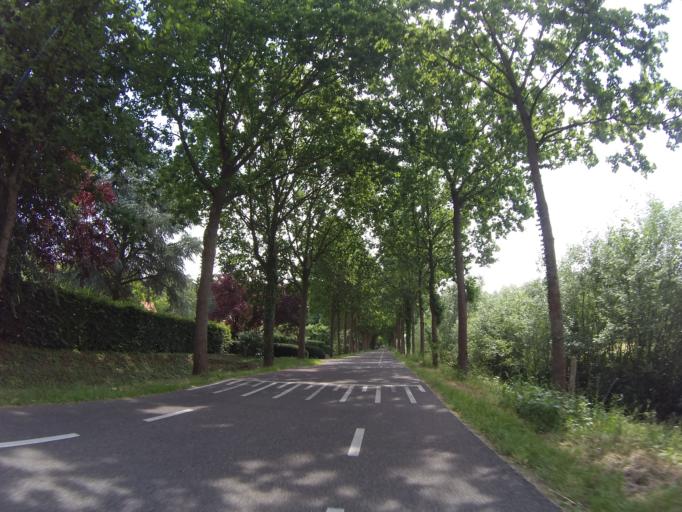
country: NL
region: Utrecht
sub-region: Gemeente Bunnik
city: Bunnik
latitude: 52.0724
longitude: 5.1992
